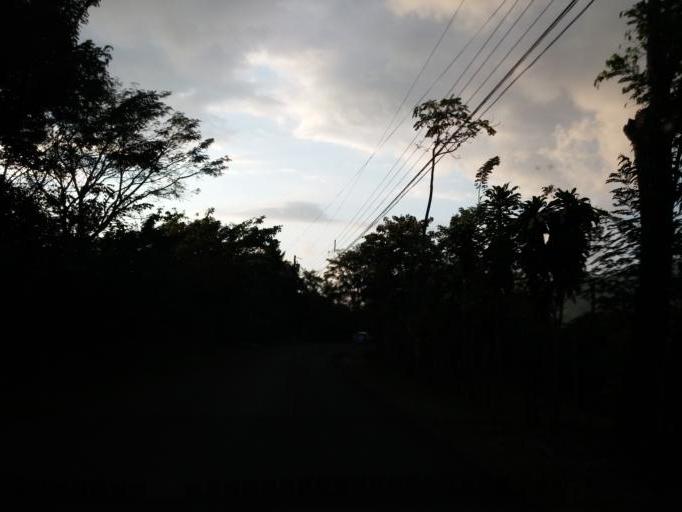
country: CR
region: San Jose
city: Palmichal
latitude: 9.8468
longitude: -84.2223
